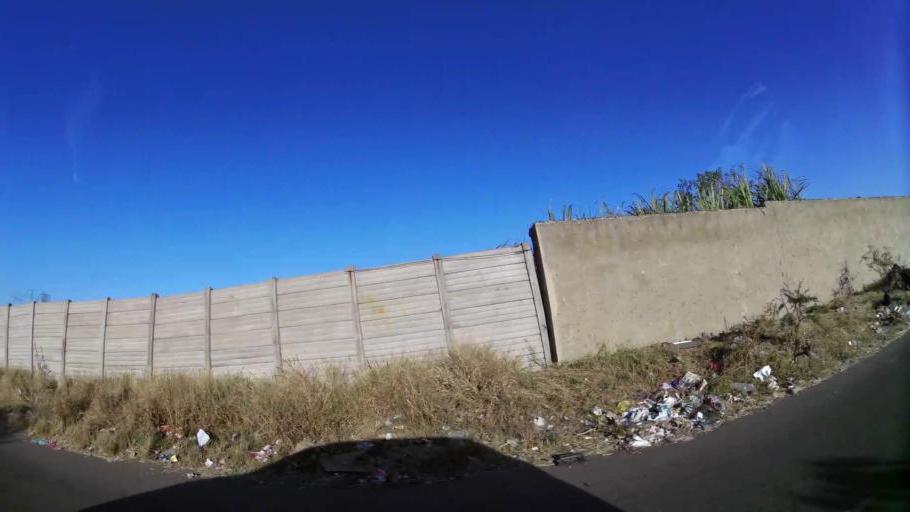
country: ZA
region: North-West
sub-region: Bojanala Platinum District Municipality
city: Rustenburg
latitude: -25.6345
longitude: 27.2207
